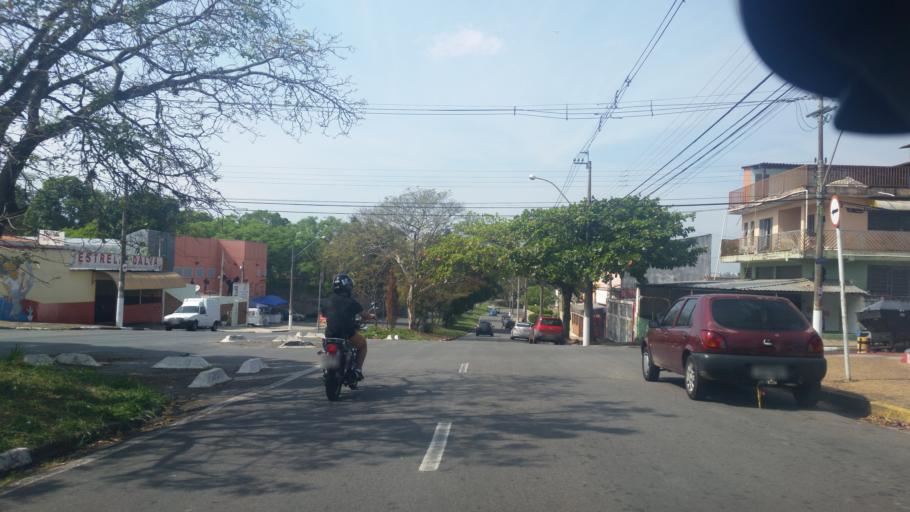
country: BR
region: Sao Paulo
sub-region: Campinas
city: Campinas
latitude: -22.8563
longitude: -47.0378
